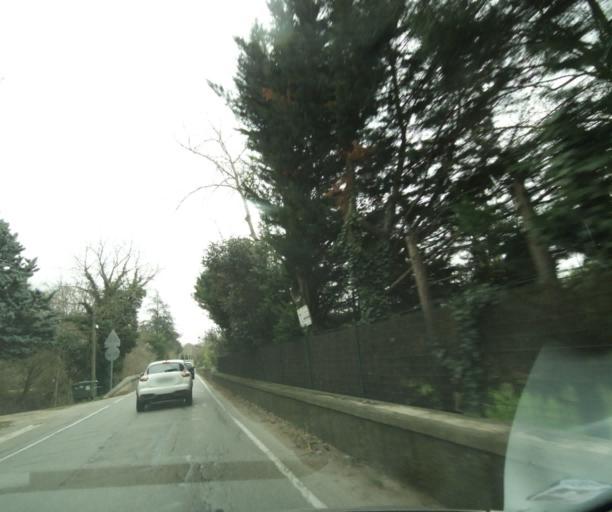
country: FR
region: Provence-Alpes-Cote d'Azur
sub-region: Departement des Bouches-du-Rhone
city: Jouques
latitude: 43.6363
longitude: 5.6234
